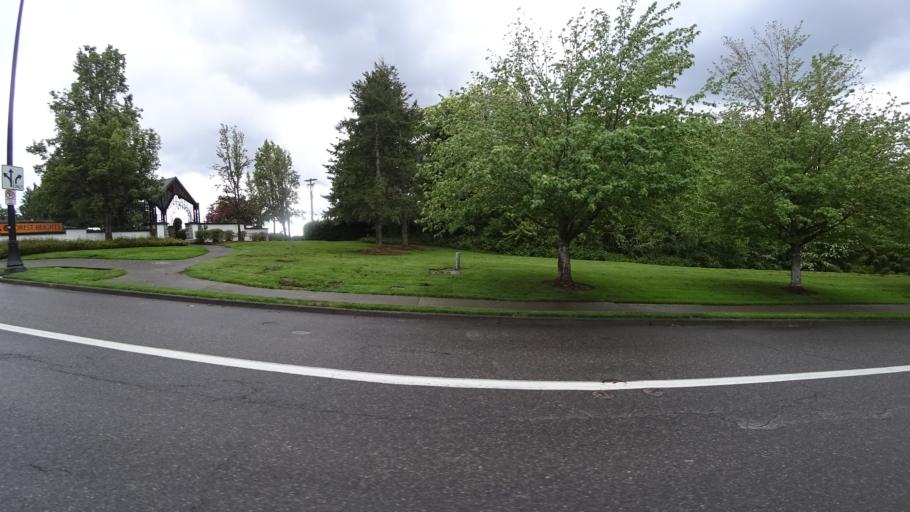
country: US
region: Oregon
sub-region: Washington County
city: West Haven
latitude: 45.5301
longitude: -122.7627
